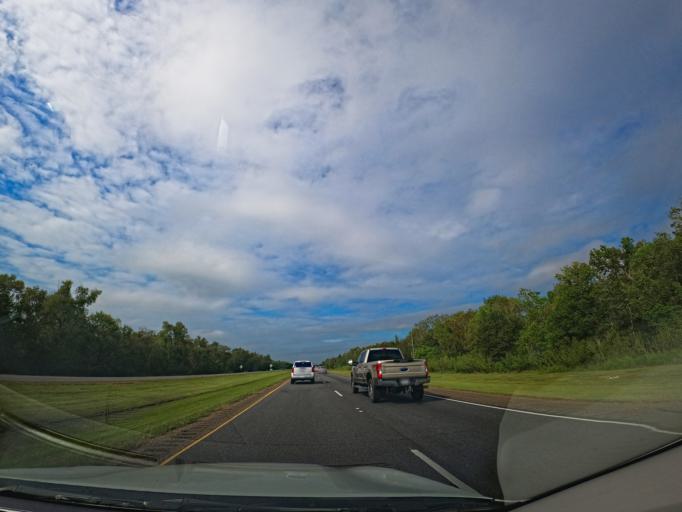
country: US
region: Louisiana
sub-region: Saint Mary Parish
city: Berwick
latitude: 29.6882
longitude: -91.2420
